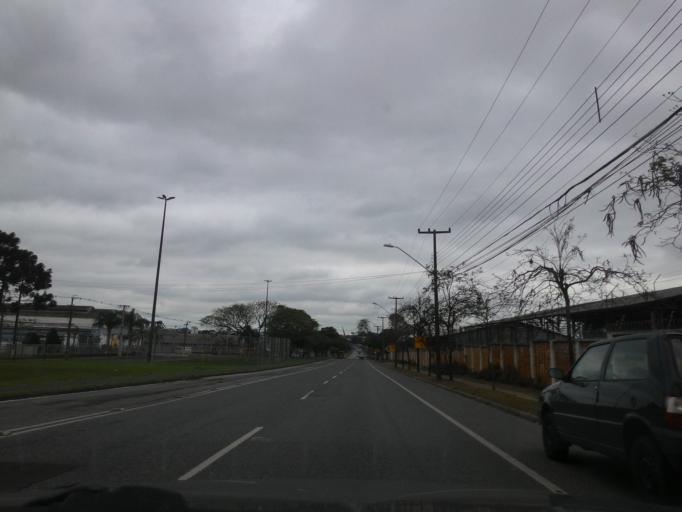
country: BR
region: Parana
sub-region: Curitiba
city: Curitiba
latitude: -25.4733
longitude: -49.2665
